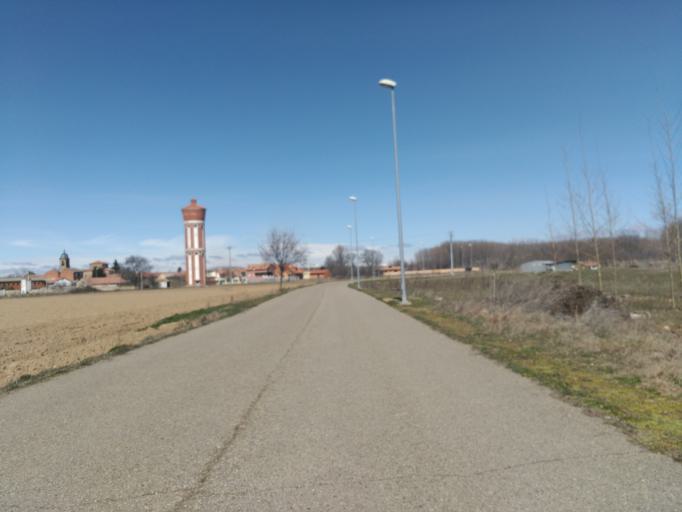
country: ES
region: Castille and Leon
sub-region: Provincia de Leon
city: Hospital de Orbigo
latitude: 42.4390
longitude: -5.8790
